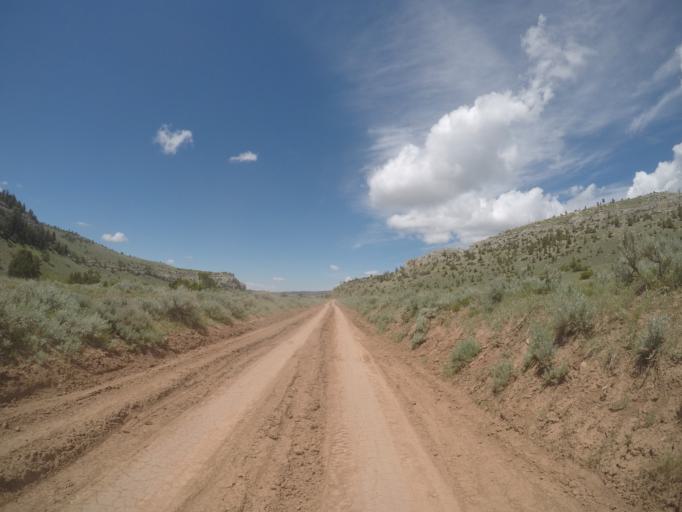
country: US
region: Wyoming
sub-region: Big Horn County
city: Lovell
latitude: 45.2331
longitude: -108.6141
